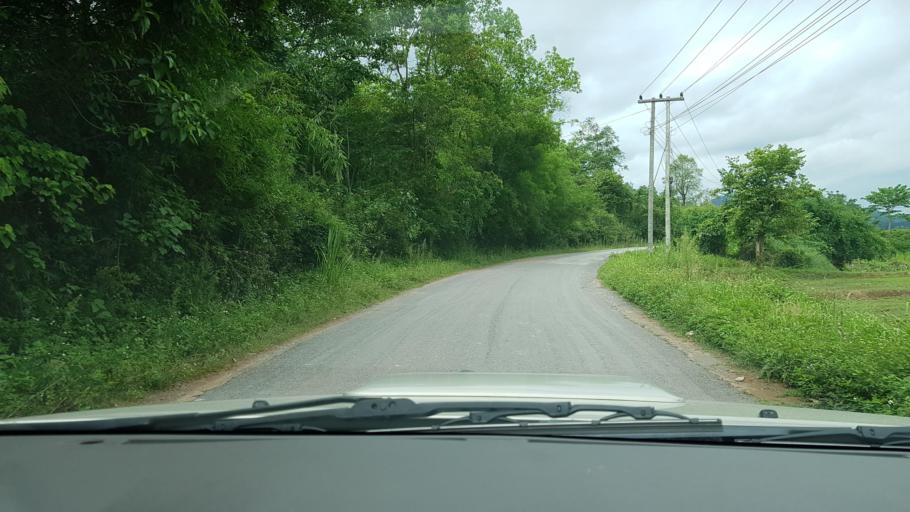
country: LA
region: Loungnamtha
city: Muang Nale
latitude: 20.4015
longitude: 101.7581
